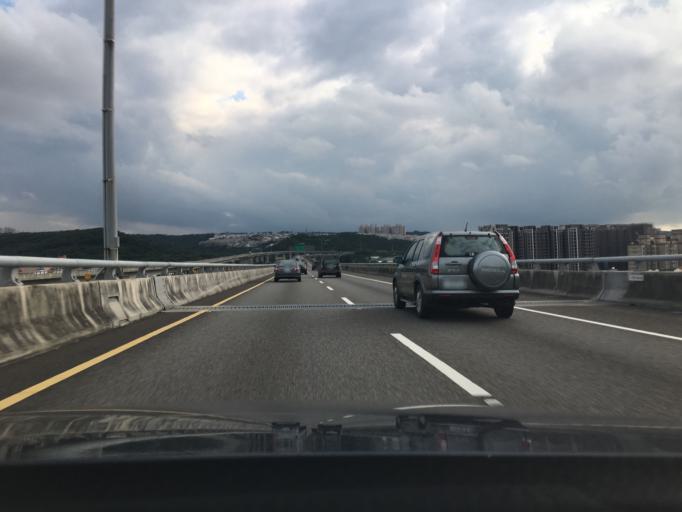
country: TW
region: Taiwan
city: Daxi
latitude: 24.9165
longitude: 121.1668
